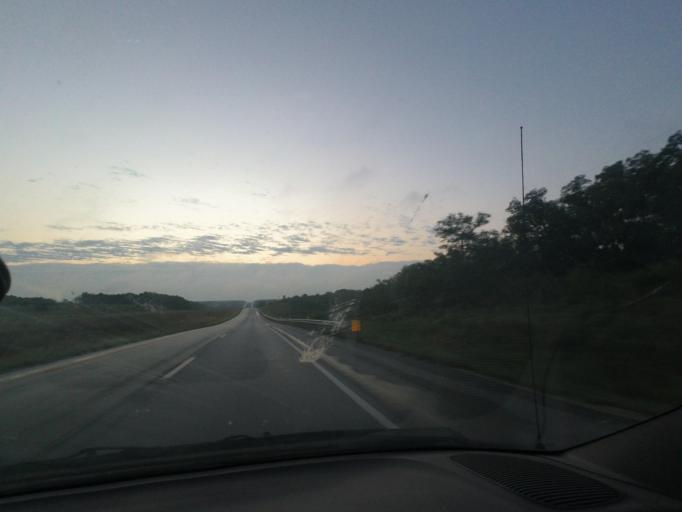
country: US
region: Missouri
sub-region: Linn County
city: Marceline
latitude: 39.7590
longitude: -92.8702
